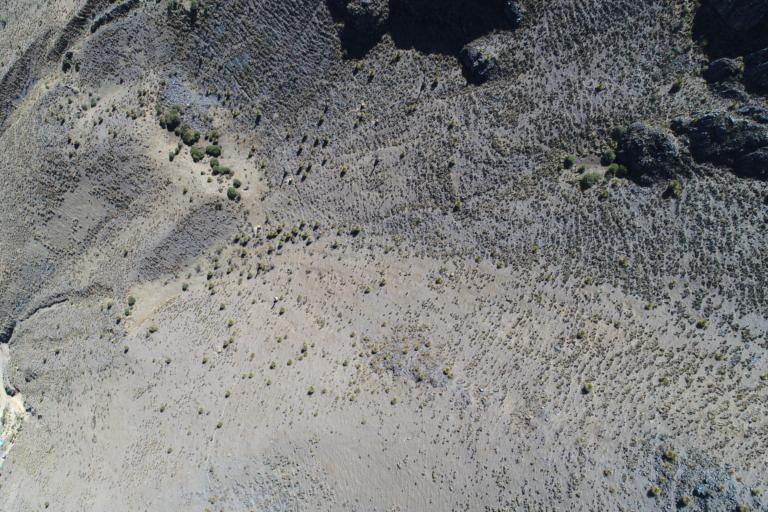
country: BO
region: La Paz
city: Viloco
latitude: -16.8105
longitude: -67.5482
